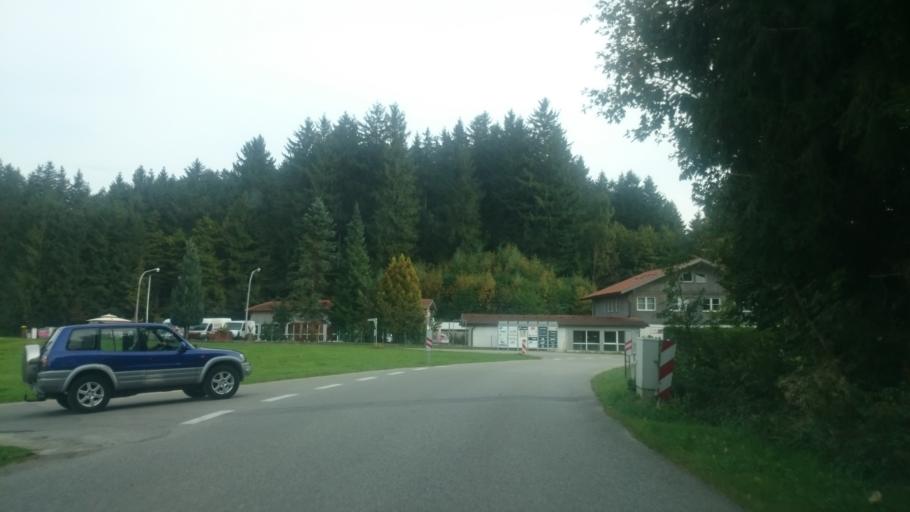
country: DE
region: Bavaria
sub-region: Swabia
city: Fuessen
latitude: 47.5788
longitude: 10.6803
